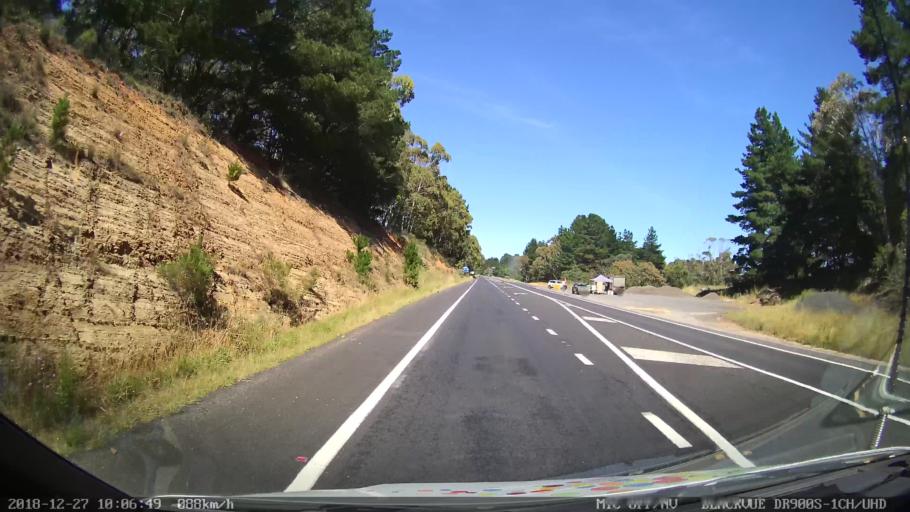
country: AU
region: New South Wales
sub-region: Lithgow
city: Portland
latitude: -33.4377
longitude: 149.8493
